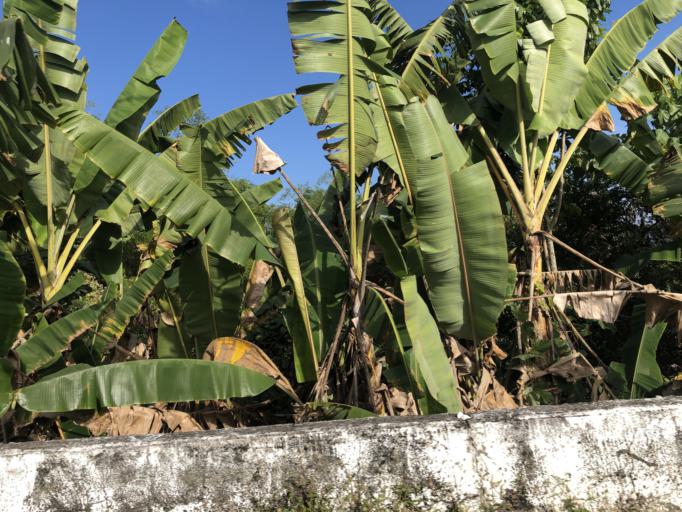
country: TW
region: Taiwan
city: Yujing
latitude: 23.0527
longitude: 120.4010
